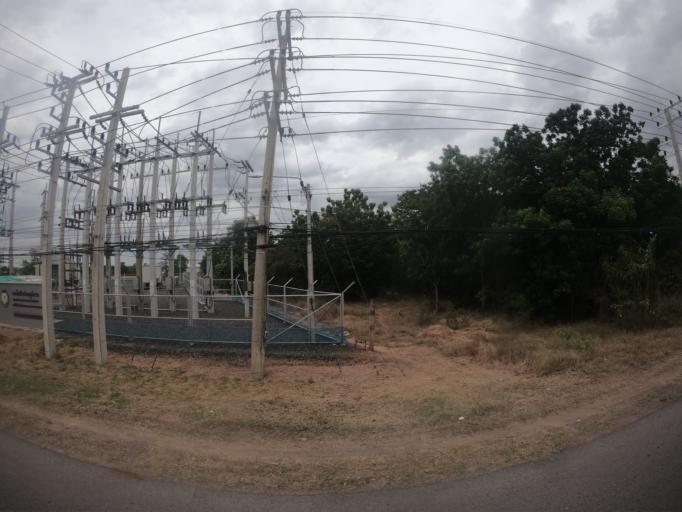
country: TH
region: Nakhon Ratchasima
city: Chok Chai
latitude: 14.8277
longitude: 102.1821
